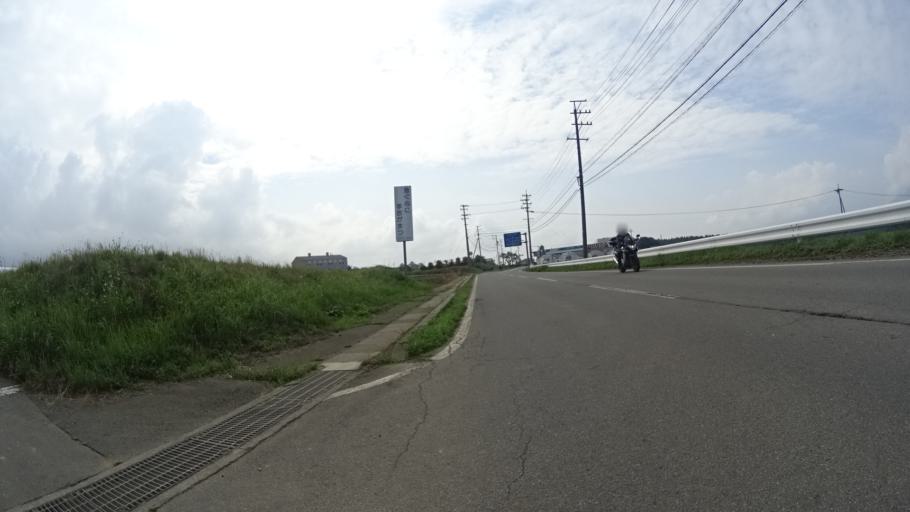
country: JP
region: Nagano
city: Chino
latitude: 35.9481
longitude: 138.2410
